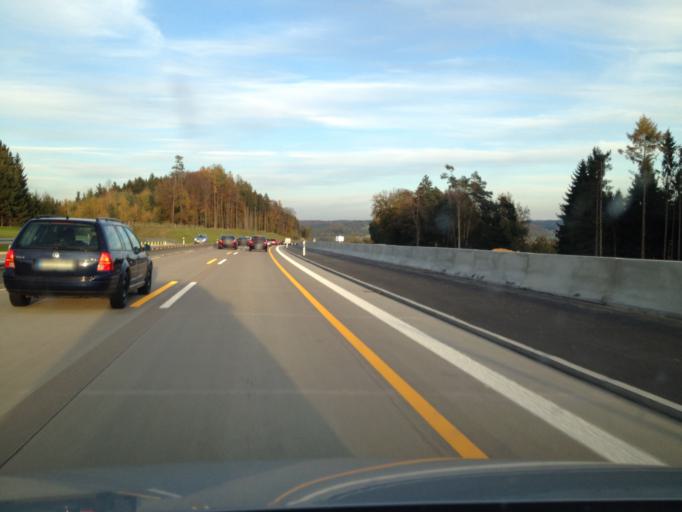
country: DE
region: Bavaria
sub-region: Swabia
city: Zusmarshausen
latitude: 48.4050
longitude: 10.5633
